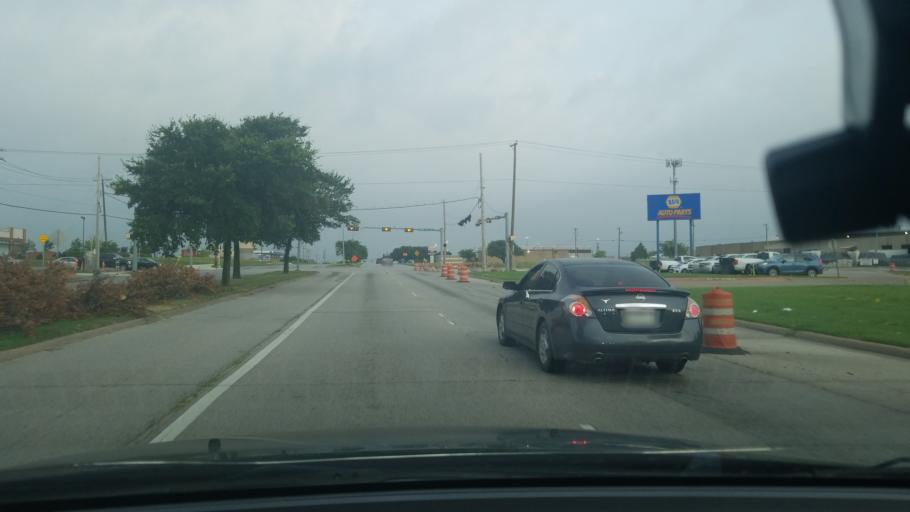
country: US
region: Texas
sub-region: Dallas County
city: Balch Springs
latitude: 32.7684
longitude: -96.6457
